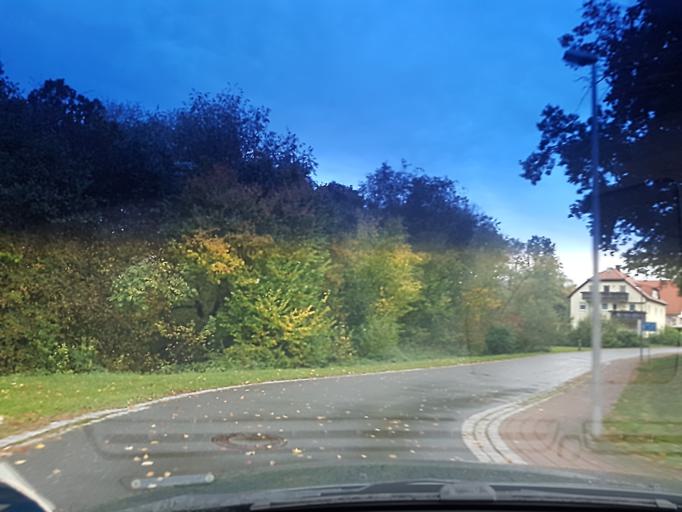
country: DE
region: Bavaria
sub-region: Regierungsbezirk Mittelfranken
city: Wachenroth
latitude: 49.7537
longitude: 10.7089
